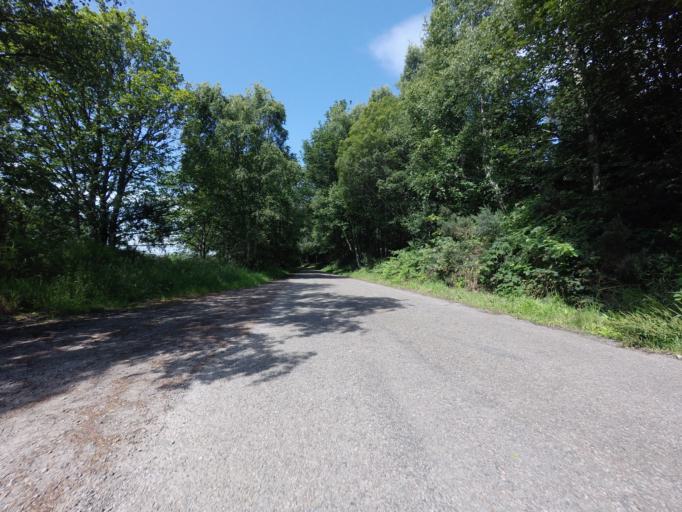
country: GB
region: Scotland
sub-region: Highland
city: Inverness
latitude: 57.5101
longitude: -4.2746
